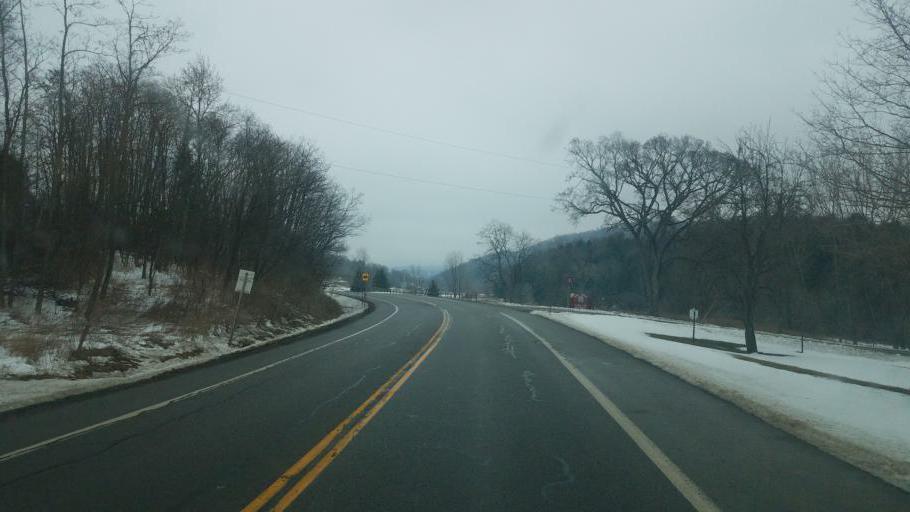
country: US
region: Pennsylvania
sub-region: Tioga County
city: Westfield
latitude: 42.0363
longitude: -77.5425
